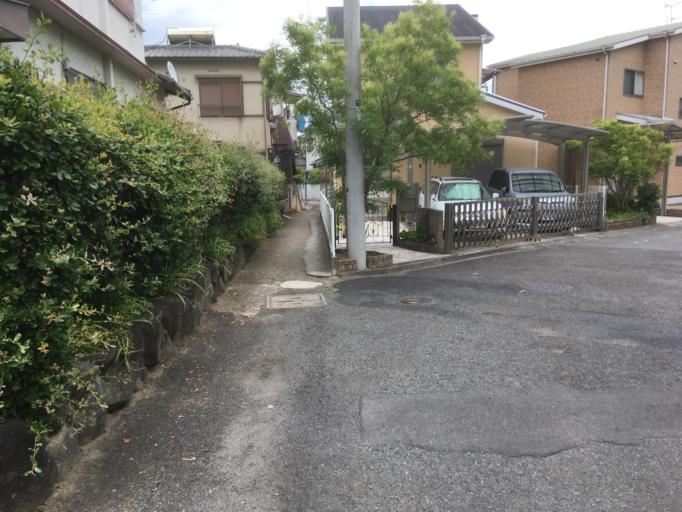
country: JP
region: Nara
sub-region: Ikoma-shi
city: Ikoma
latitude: 34.6750
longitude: 135.7021
